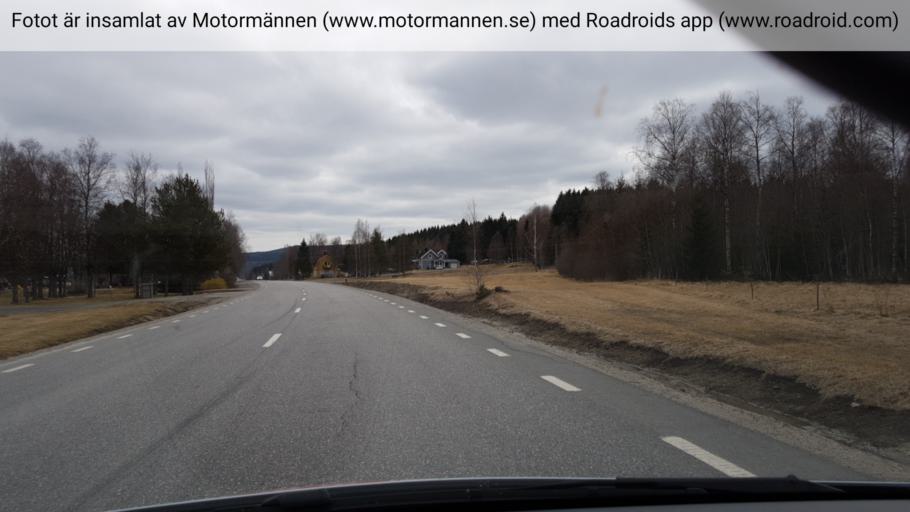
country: SE
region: Vaesternorrland
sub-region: OErnskoeldsviks Kommun
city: Ornskoldsvik
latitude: 63.3335
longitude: 18.6733
